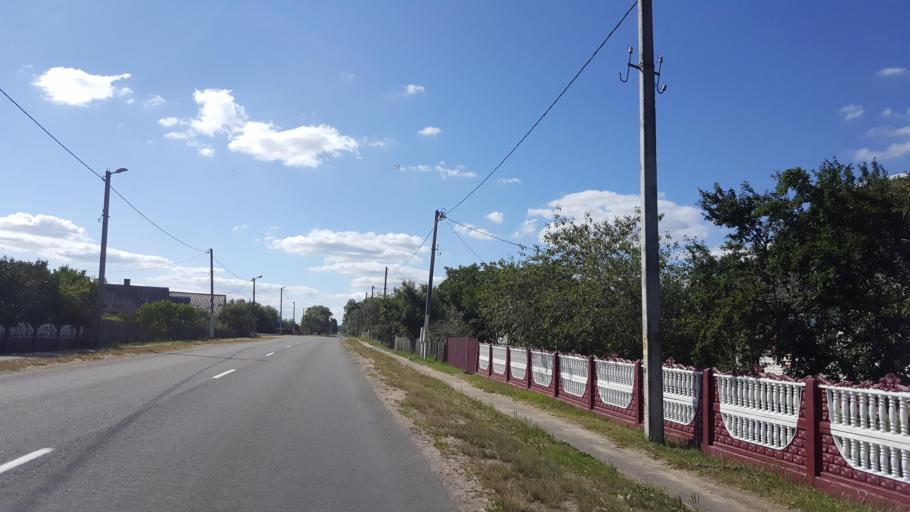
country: BY
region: Brest
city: Kobryn
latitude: 52.3414
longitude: 24.2334
